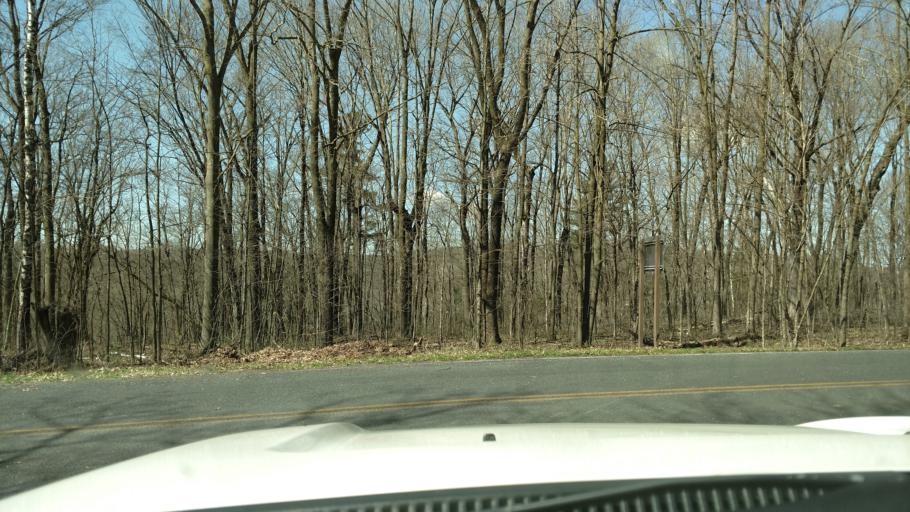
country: US
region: Wisconsin
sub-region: Pierce County
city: Spring Valley
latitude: 44.8699
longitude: -92.2444
